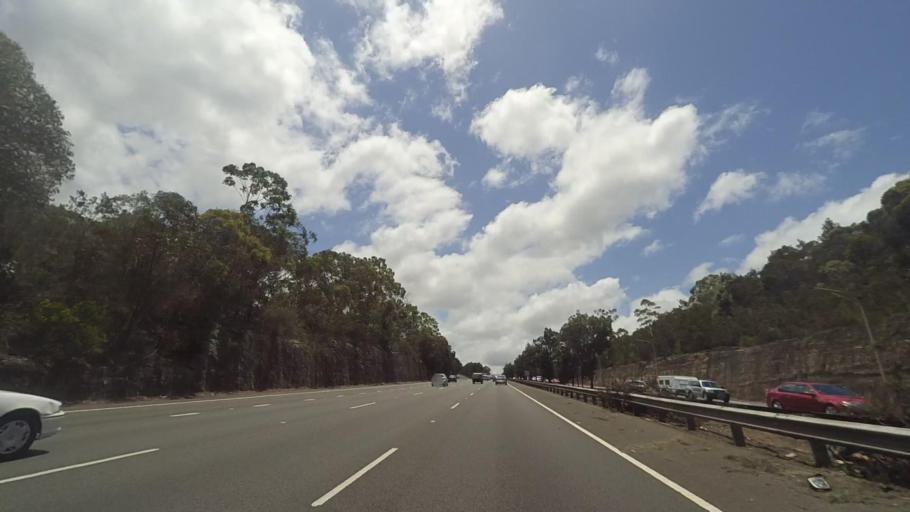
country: AU
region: New South Wales
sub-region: Hornsby Shire
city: Mount Colah
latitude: -33.6849
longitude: 151.1207
